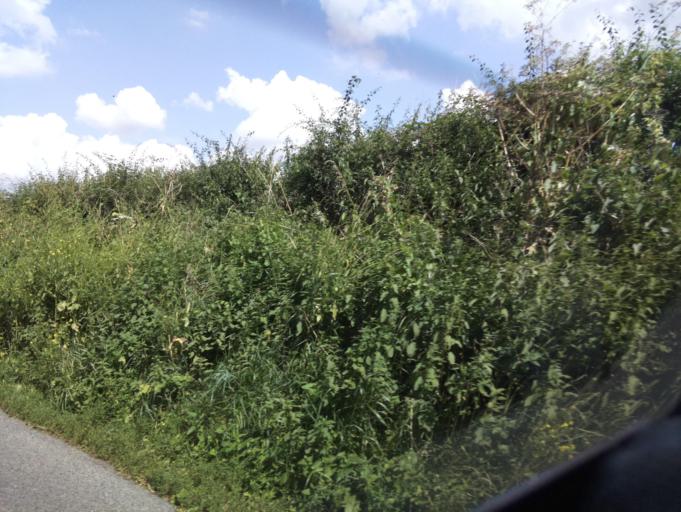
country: GB
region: England
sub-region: Wiltshire
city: Malmesbury
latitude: 51.5730
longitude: -2.0767
